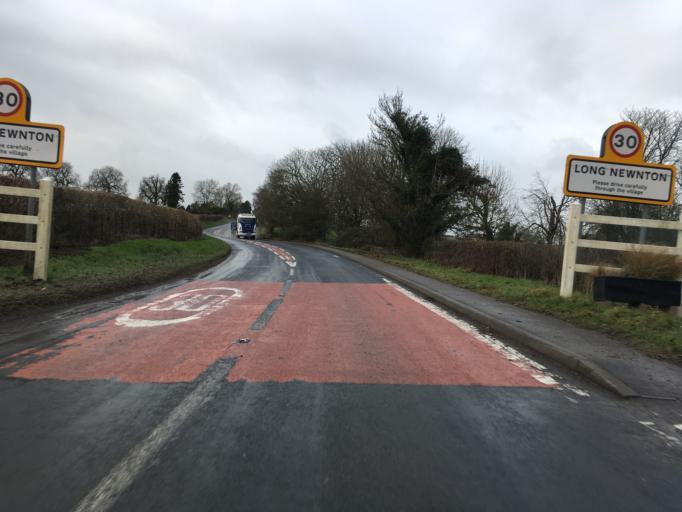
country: GB
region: England
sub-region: Gloucestershire
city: Tetbury
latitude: 51.6256
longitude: -2.1307
